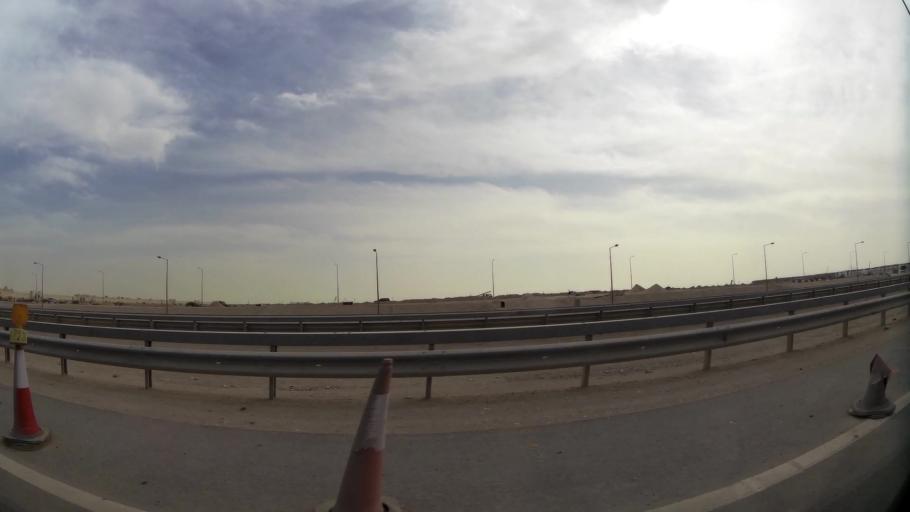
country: QA
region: Baladiyat ar Rayyan
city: Ar Rayyan
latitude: 25.3236
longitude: 51.3467
